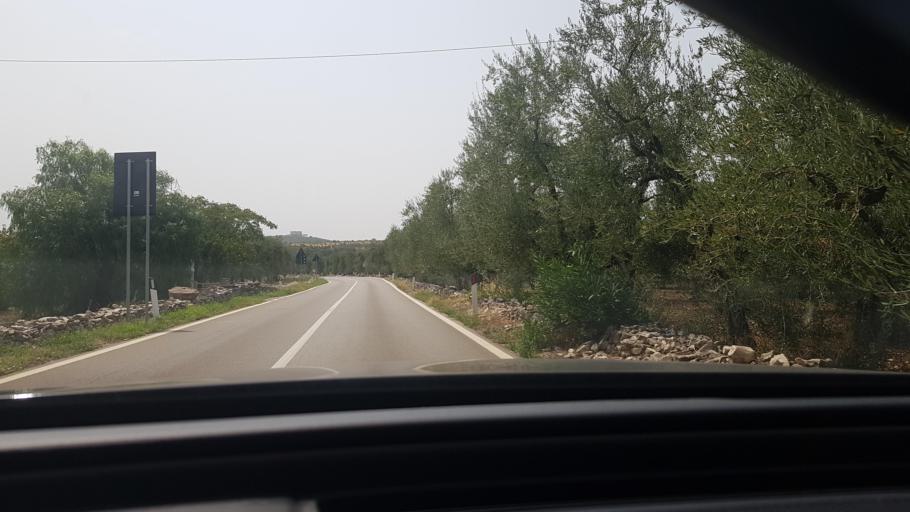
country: IT
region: Apulia
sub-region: Provincia di Barletta - Andria - Trani
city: Andria
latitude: 41.1145
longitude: 16.2817
